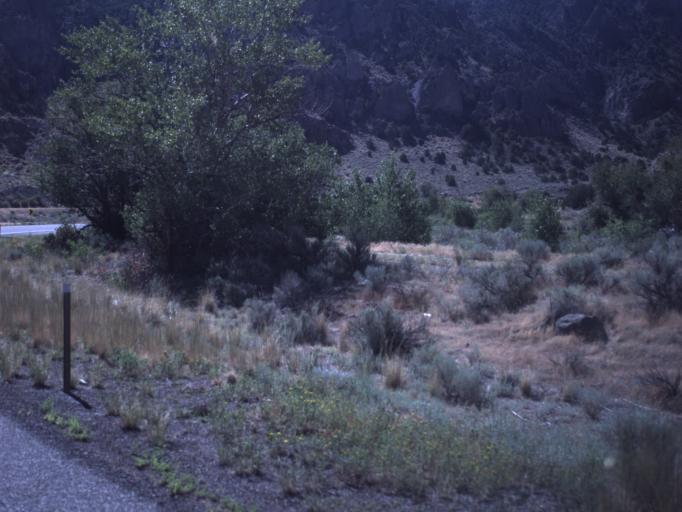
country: US
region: Utah
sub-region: Sevier County
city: Monroe
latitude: 38.5711
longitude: -112.2544
